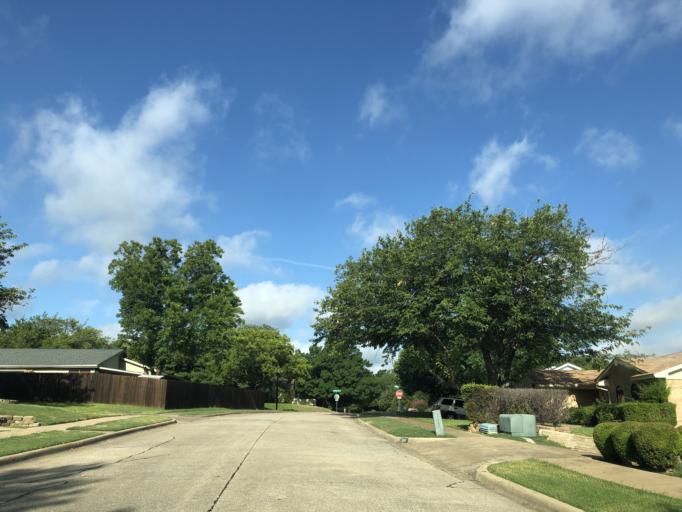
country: US
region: Texas
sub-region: Dallas County
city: Garland
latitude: 32.8643
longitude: -96.6332
